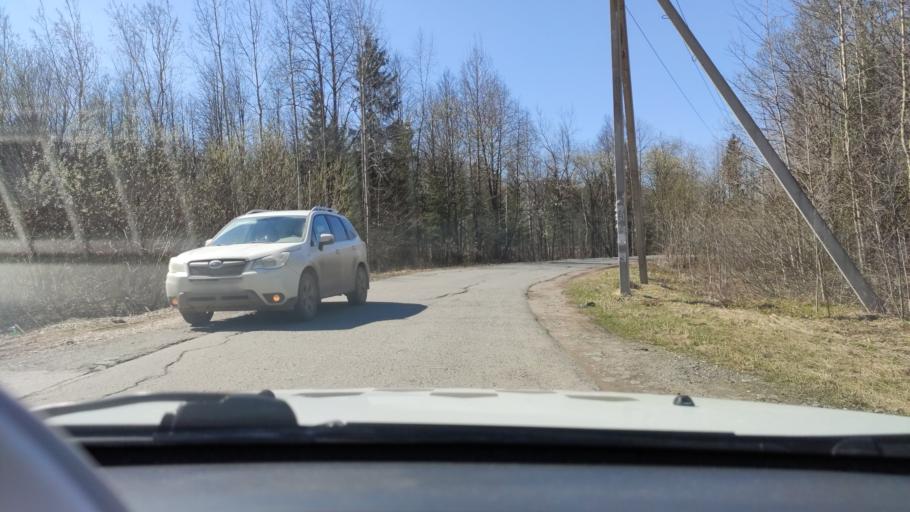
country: RU
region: Perm
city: Novyye Lyady
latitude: 58.0401
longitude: 56.6258
